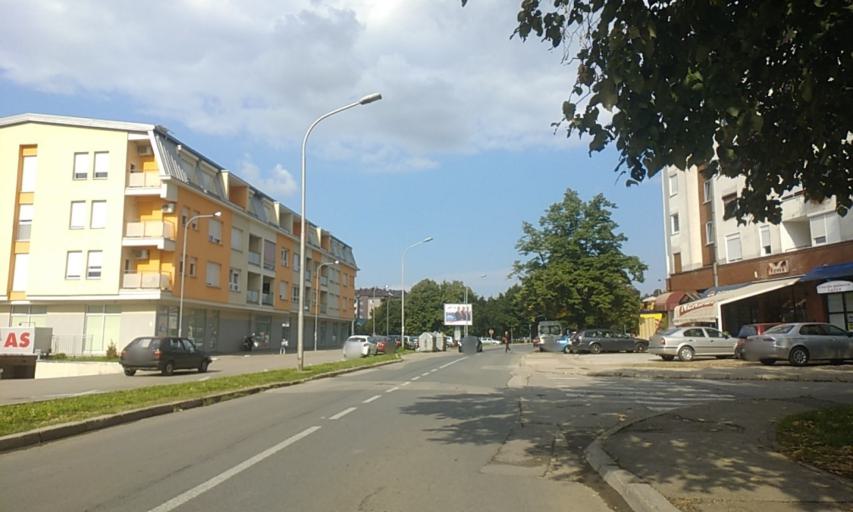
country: BA
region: Republika Srpska
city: Mejdan - Obilicevo
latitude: 44.7610
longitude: 17.2004
